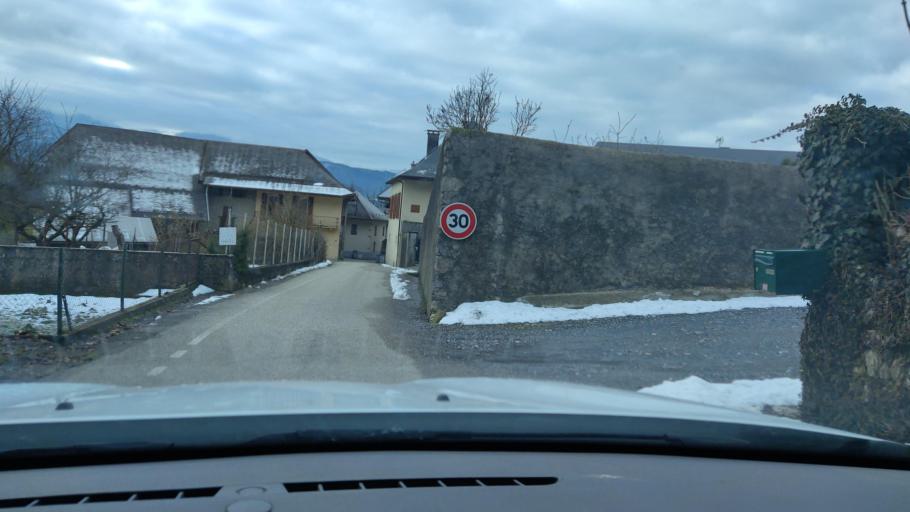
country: FR
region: Rhone-Alpes
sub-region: Departement de la Savoie
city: Coise-Saint-Jean-Pied-Gauthier
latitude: 45.5589
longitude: 6.1284
